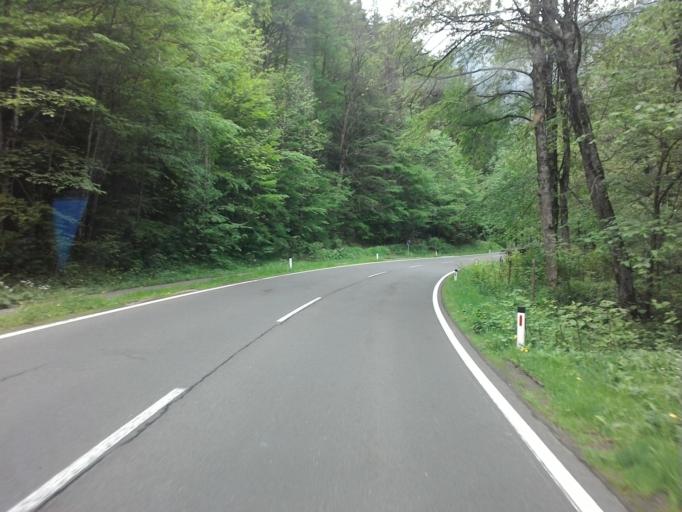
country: AT
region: Styria
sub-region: Politischer Bezirk Leoben
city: Eisenerz
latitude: 47.5772
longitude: 14.8278
